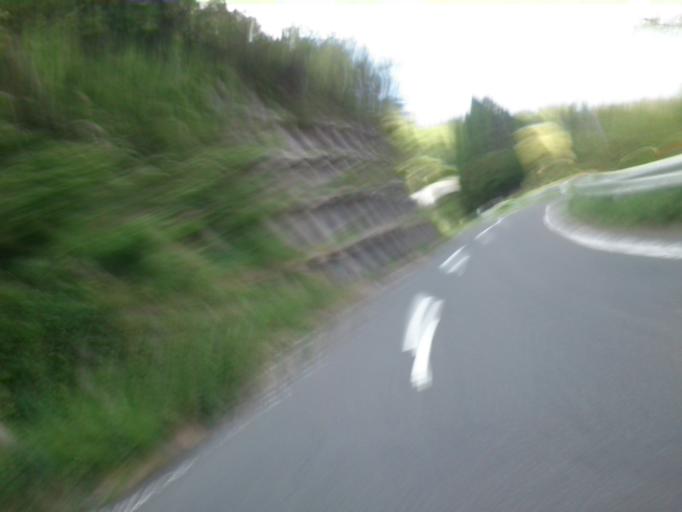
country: JP
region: Kyoto
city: Miyazu
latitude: 35.6879
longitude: 135.1574
